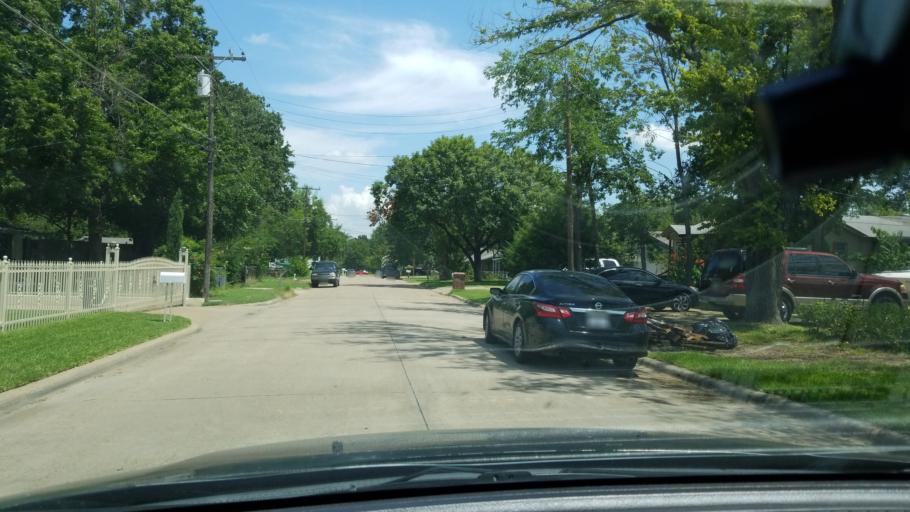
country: US
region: Texas
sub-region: Dallas County
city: Balch Springs
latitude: 32.7493
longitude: -96.6259
